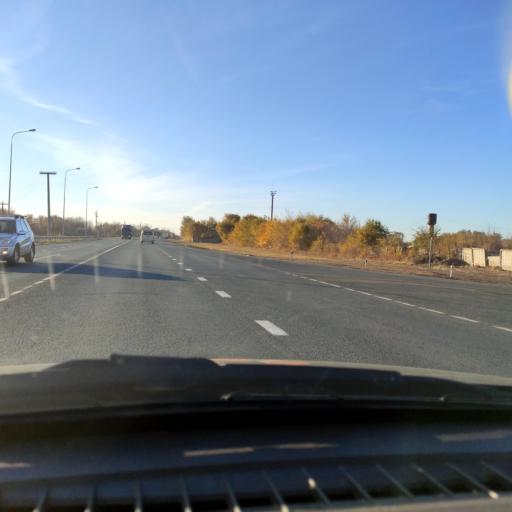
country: RU
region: Samara
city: Varlamovo
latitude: 53.1917
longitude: 48.3434
